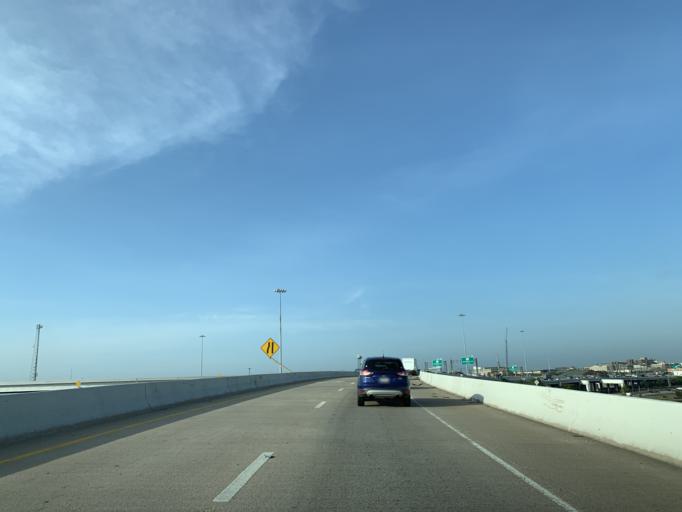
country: US
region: Texas
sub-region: Tarrant County
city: Fort Worth
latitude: 32.7477
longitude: -97.3213
